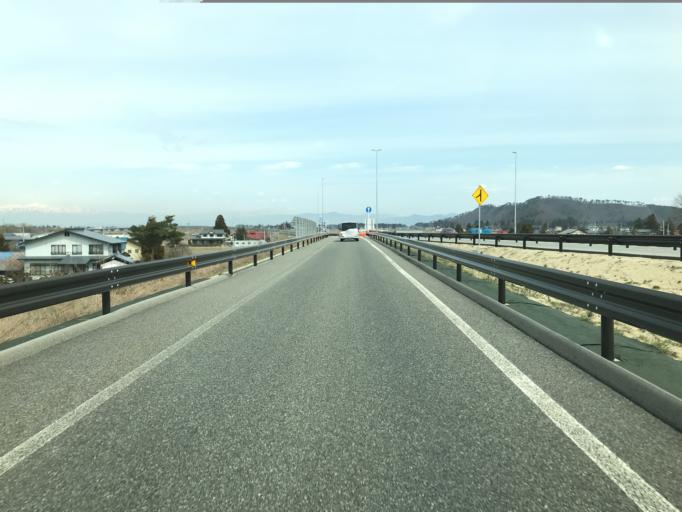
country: JP
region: Yamagata
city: Yonezawa
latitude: 37.9236
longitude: 140.1351
